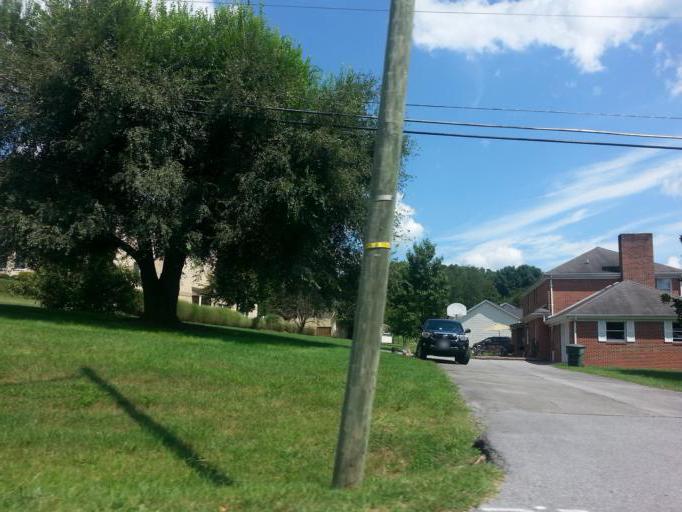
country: US
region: Virginia
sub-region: Washington County
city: Abingdon
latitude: 36.6956
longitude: -81.9736
